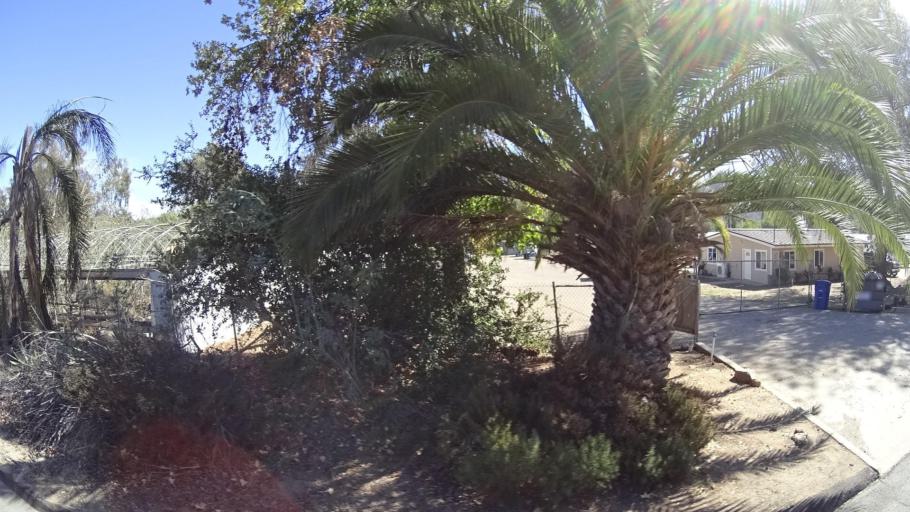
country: US
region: California
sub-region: San Diego County
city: Harbison Canyon
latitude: 32.8609
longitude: -116.8580
